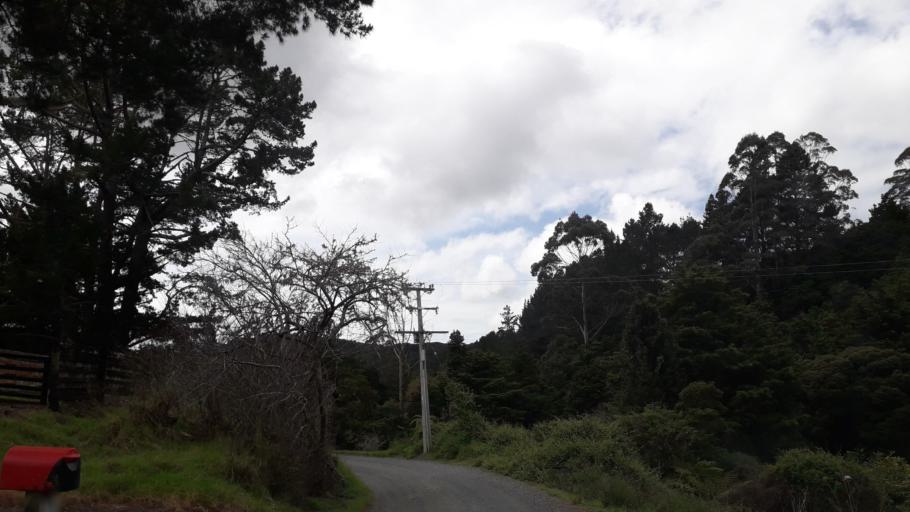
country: NZ
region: Northland
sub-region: Far North District
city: Taipa
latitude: -35.0762
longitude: 173.5538
